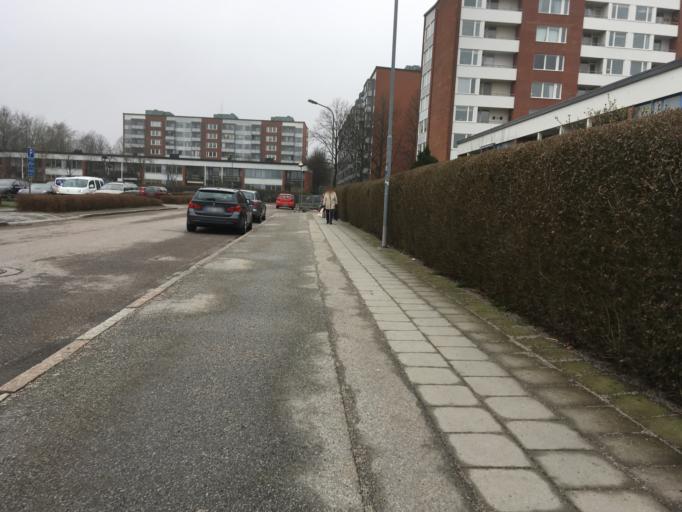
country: SE
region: Skane
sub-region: Lunds Kommun
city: Lund
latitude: 55.6906
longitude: 13.1805
